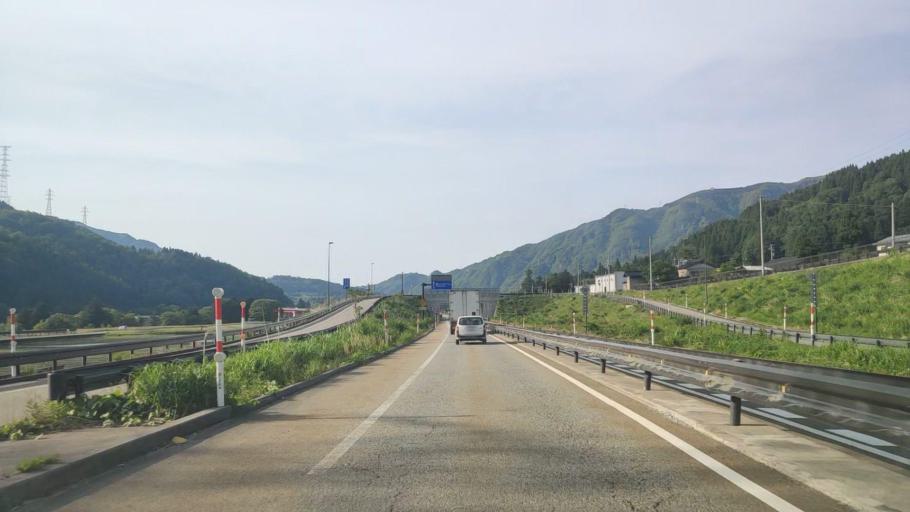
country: JP
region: Toyama
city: Yatsuomachi-higashikumisaka
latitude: 36.5198
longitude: 137.2311
